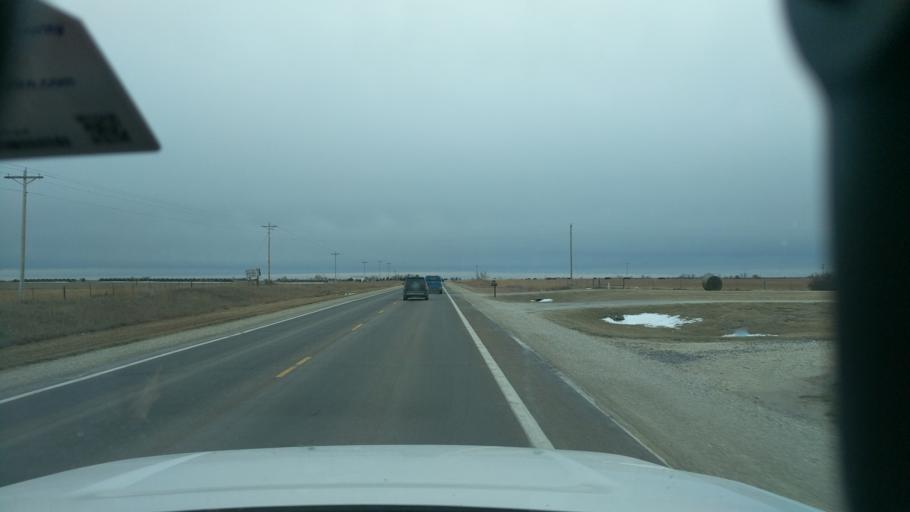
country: US
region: Kansas
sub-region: Dickinson County
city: Herington
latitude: 38.6228
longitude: -96.9487
